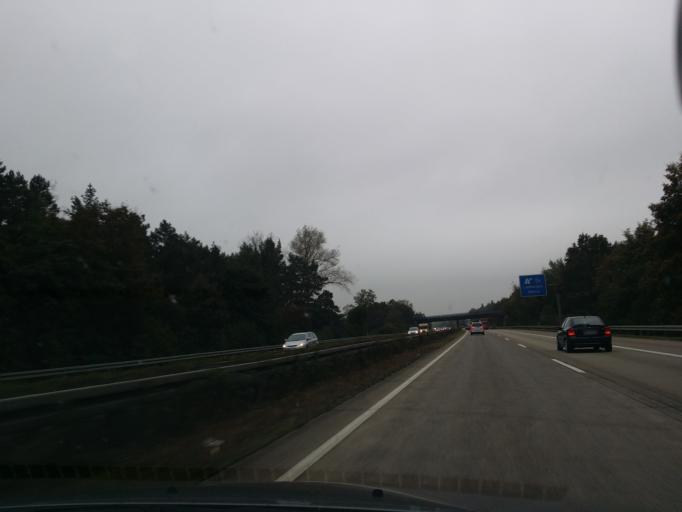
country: DE
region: North Rhine-Westphalia
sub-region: Regierungsbezirk Munster
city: Ladbergen
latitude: 52.1580
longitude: 7.7435
